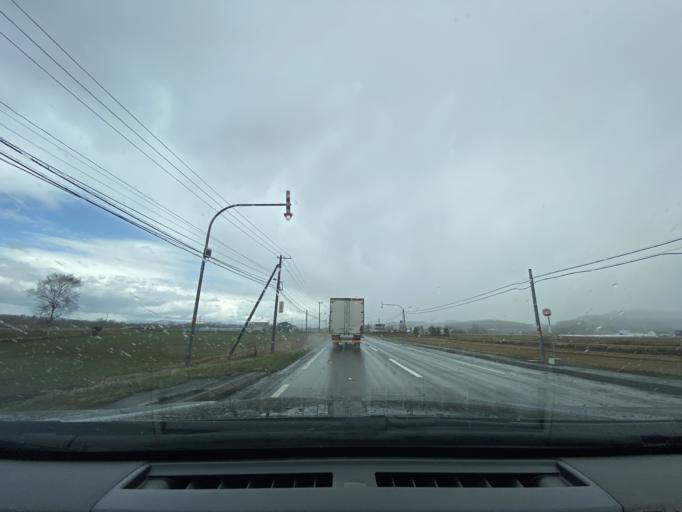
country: JP
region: Hokkaido
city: Fukagawa
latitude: 43.6685
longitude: 142.0097
